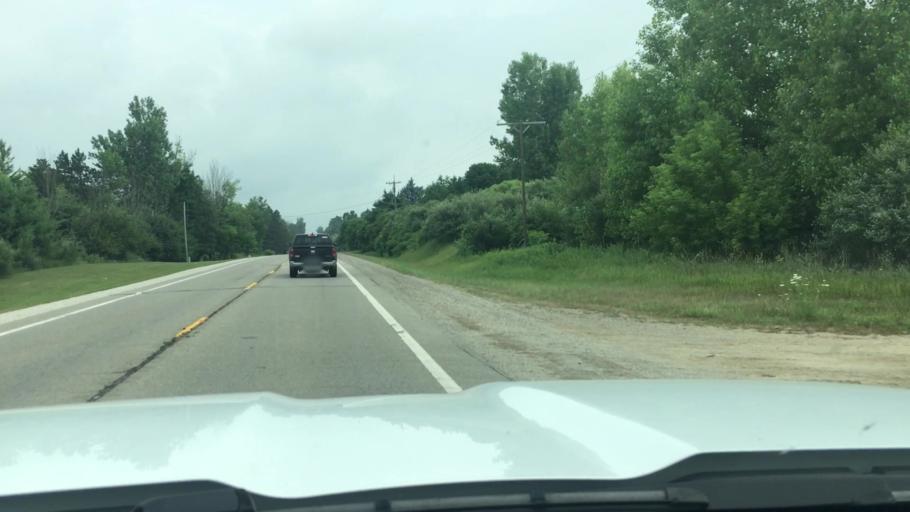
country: US
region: Michigan
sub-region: Sanilac County
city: Brown City
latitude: 43.1733
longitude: -83.0760
